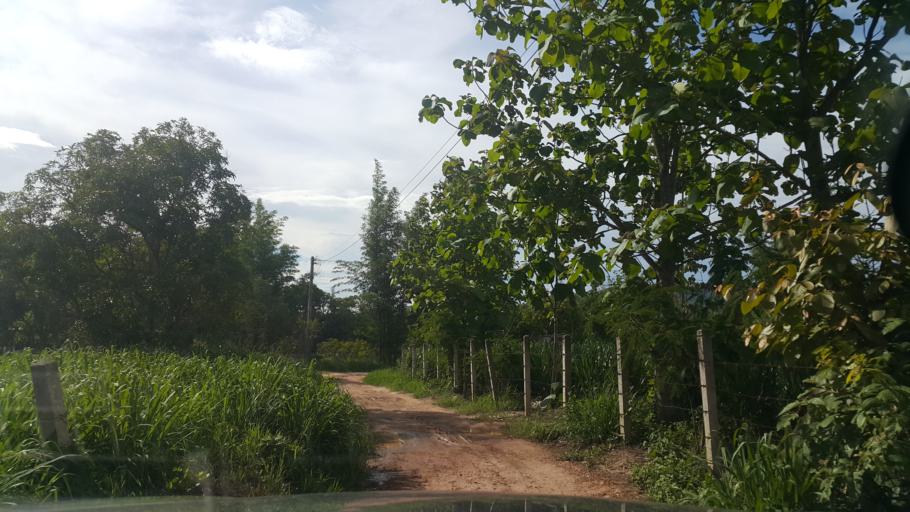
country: TH
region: Chiang Mai
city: Mae On
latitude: 18.7148
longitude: 99.2120
